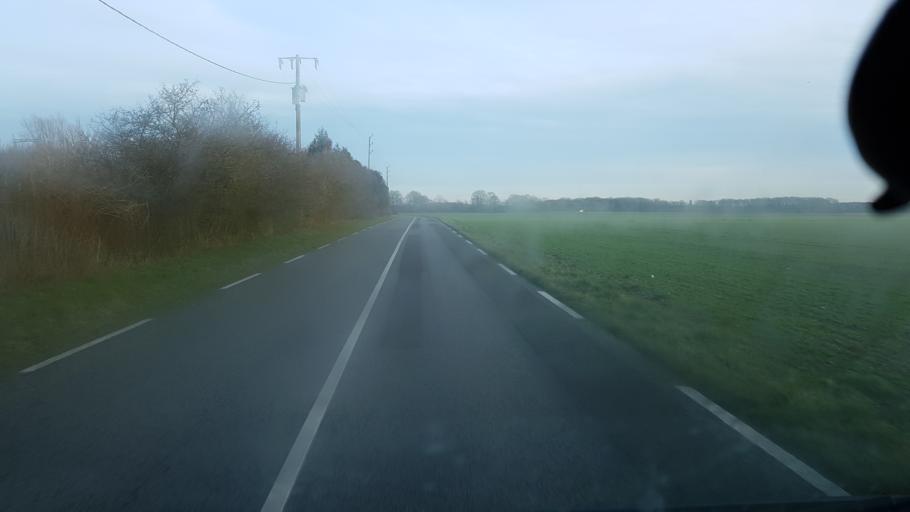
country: FR
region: Ile-de-France
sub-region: Departement des Yvelines
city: Auffargis
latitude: 48.6834
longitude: 1.8781
